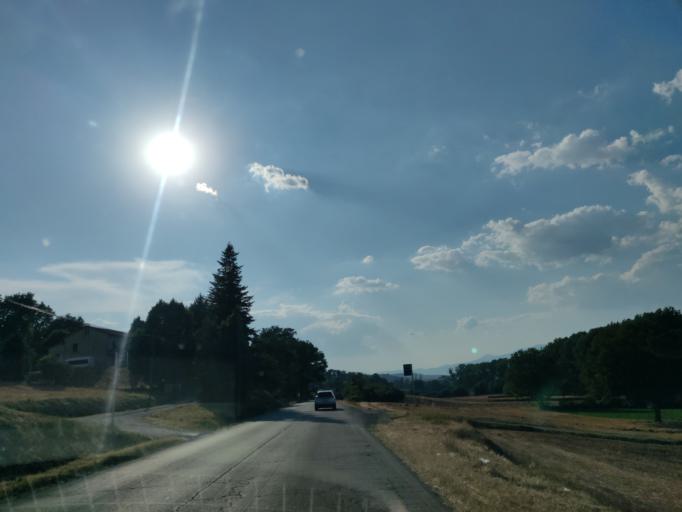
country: IT
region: Latium
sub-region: Provincia di Viterbo
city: Acquapendente
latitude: 42.7612
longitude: 11.8610
